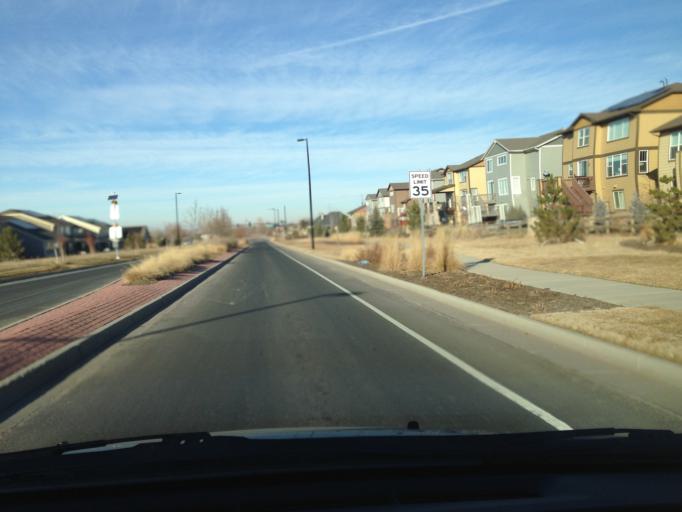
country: US
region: Colorado
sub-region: Boulder County
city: Erie
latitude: 40.0342
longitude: -105.0859
